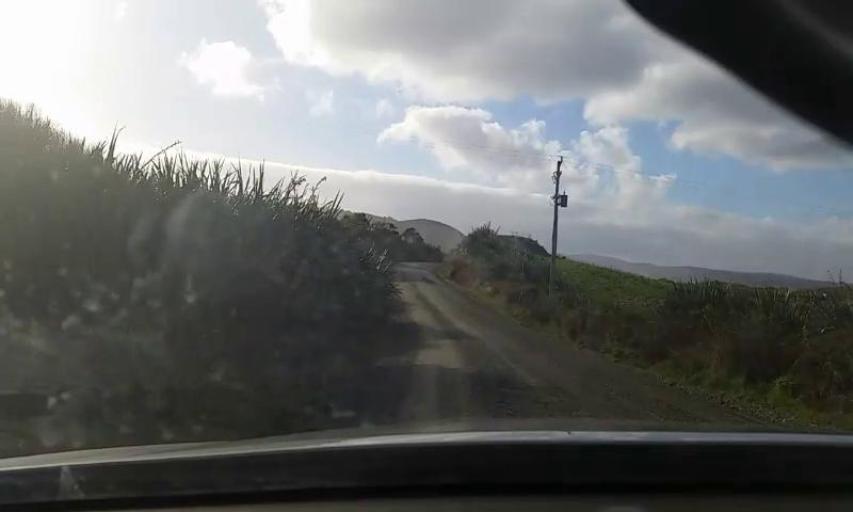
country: NZ
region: Otago
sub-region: Clutha District
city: Papatowai
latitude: -46.6515
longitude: 169.0976
